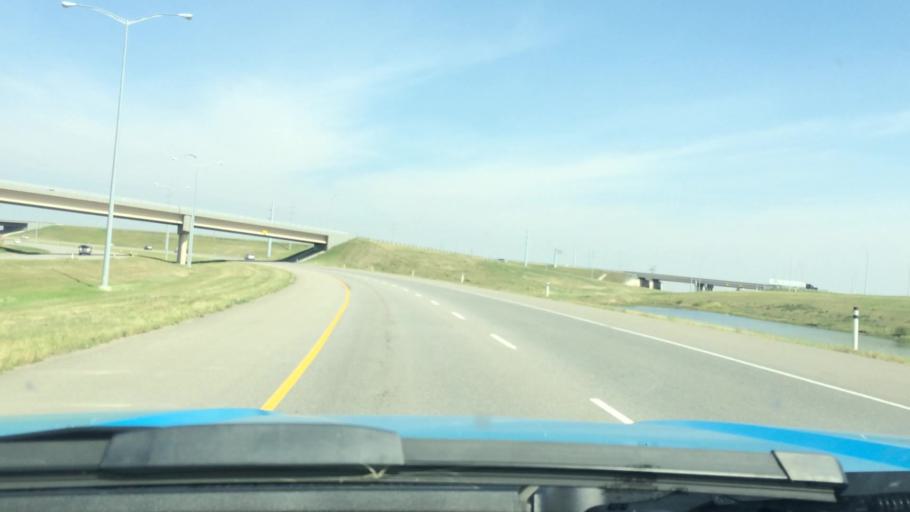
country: CA
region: Alberta
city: Chestermere
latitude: 50.9066
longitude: -113.9142
